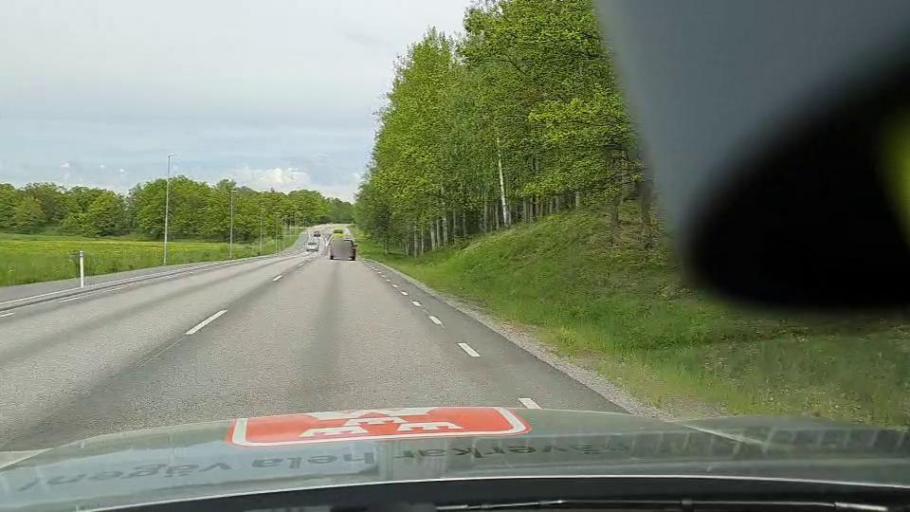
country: SE
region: Soedermanland
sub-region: Flens Kommun
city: Flen
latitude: 59.0763
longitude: 16.5960
